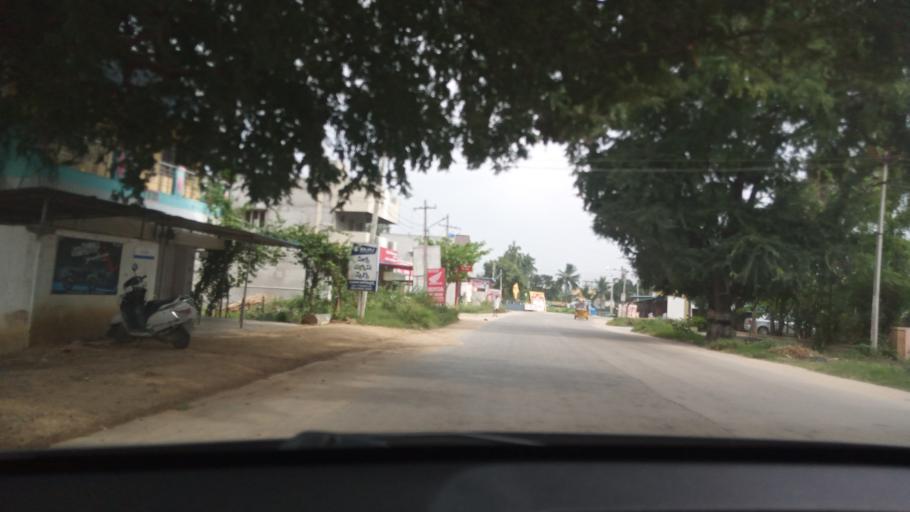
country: IN
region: Andhra Pradesh
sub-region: Chittoor
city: Madanapalle
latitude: 13.6527
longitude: 78.8073
